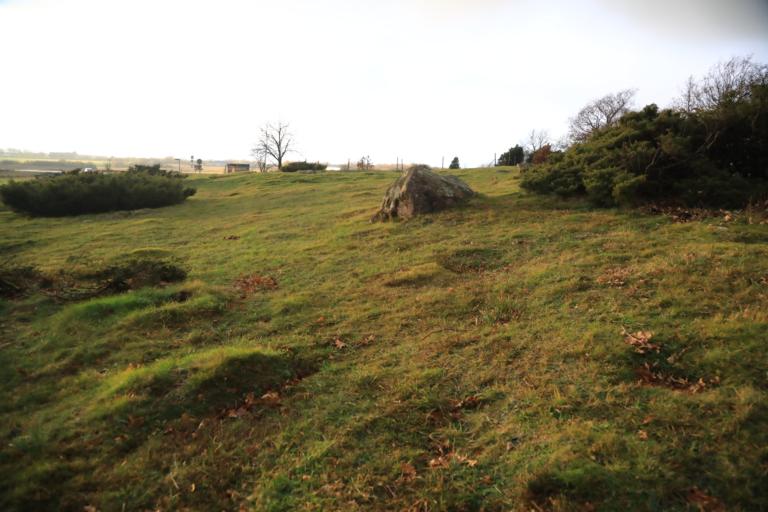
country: SE
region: Halland
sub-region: Varbergs Kommun
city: Traslovslage
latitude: 57.1125
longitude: 12.3208
